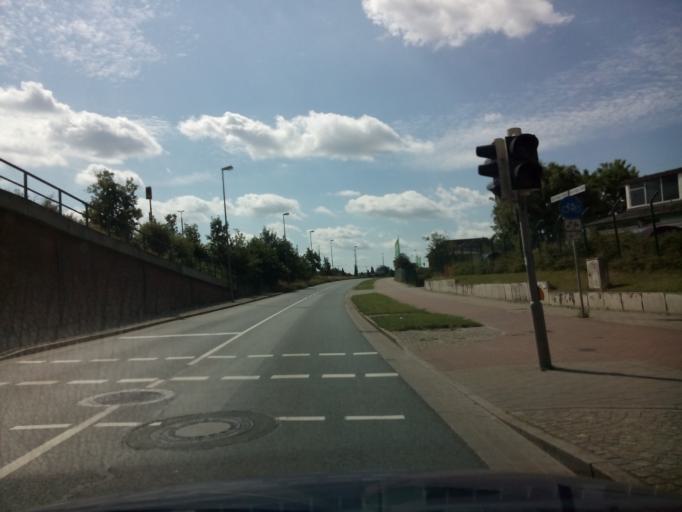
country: DE
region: Lower Saxony
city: Ritterhude
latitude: 53.1196
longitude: 8.7508
